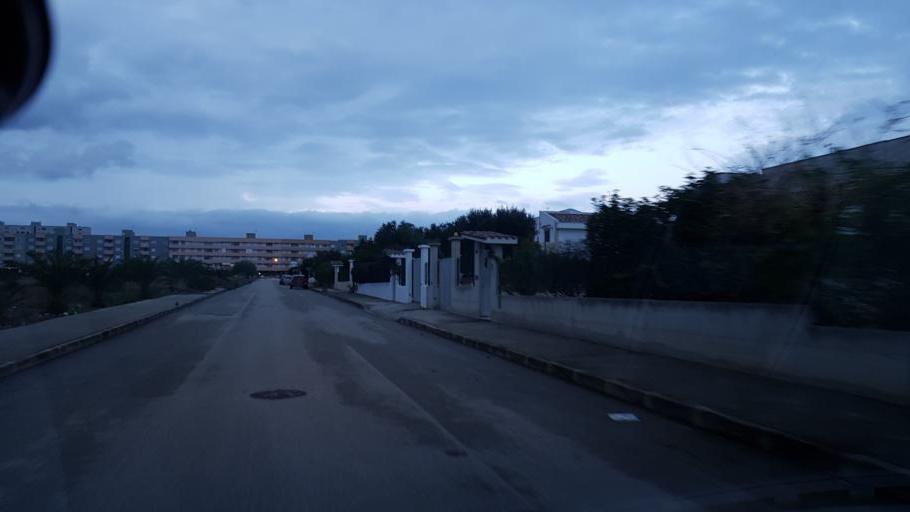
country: IT
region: Apulia
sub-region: Provincia di Taranto
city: Paolo VI
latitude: 40.5286
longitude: 17.2848
